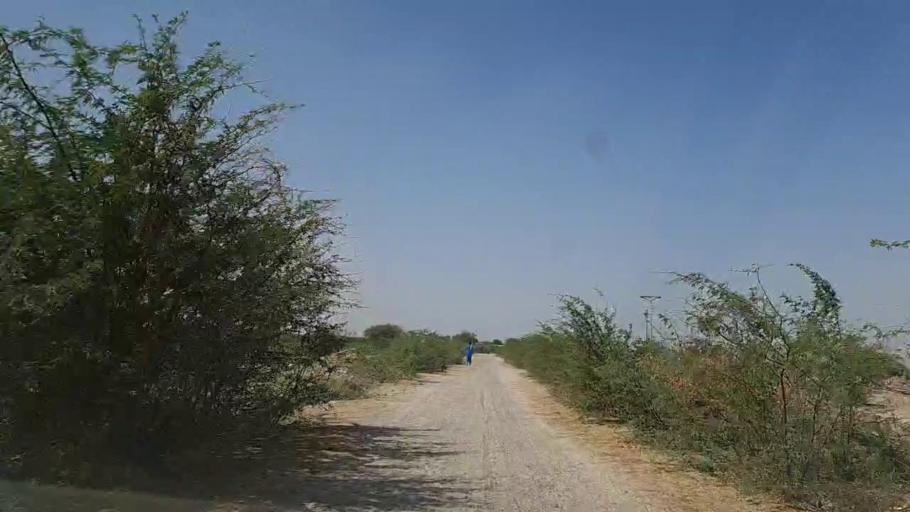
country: PK
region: Sindh
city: Naukot
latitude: 24.6216
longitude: 69.2906
